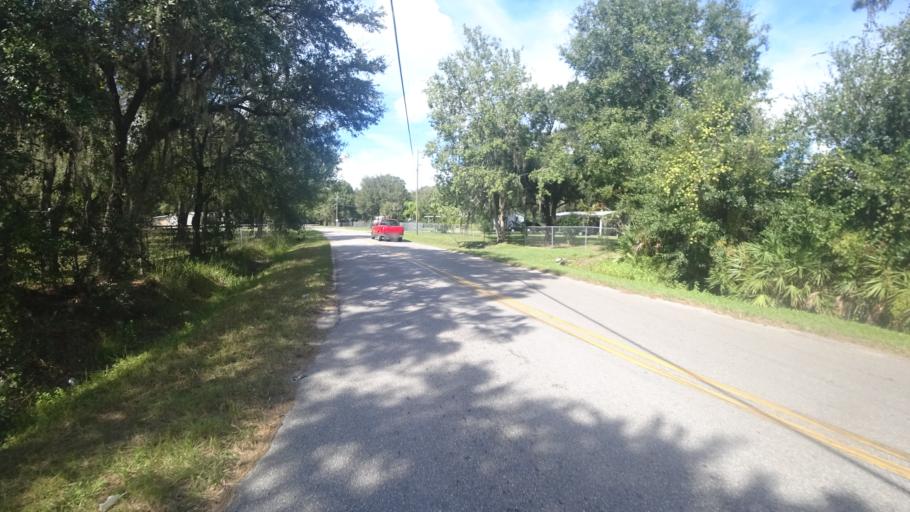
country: US
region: Florida
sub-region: Hillsborough County
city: Sun City Center
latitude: 27.6570
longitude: -82.3620
